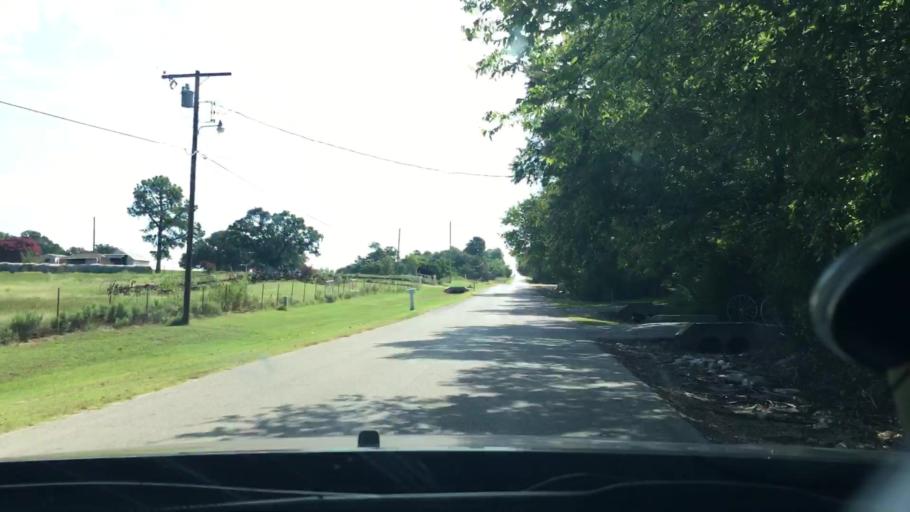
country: US
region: Oklahoma
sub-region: Carter County
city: Ardmore
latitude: 34.1436
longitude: -97.0834
